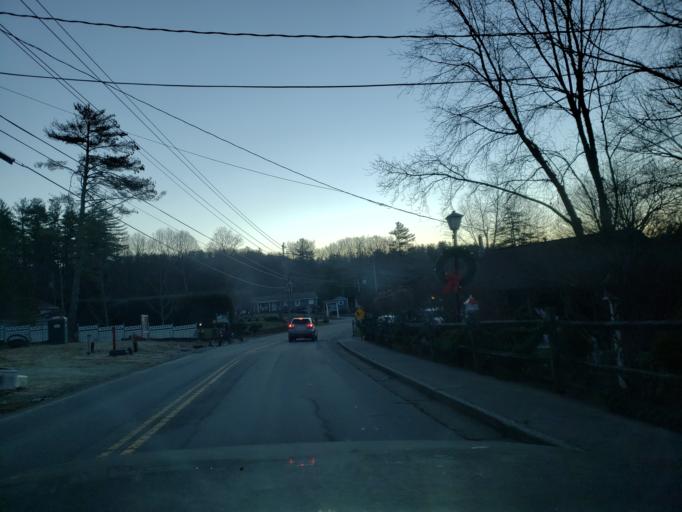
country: US
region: North Carolina
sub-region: Watauga County
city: Blowing Rock
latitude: 36.1353
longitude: -81.6769
